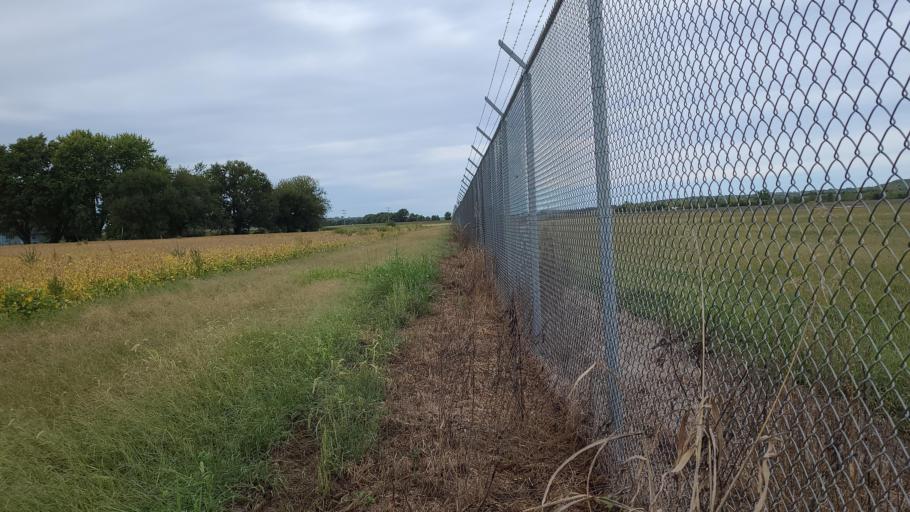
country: US
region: Kansas
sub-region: Douglas County
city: Lawrence
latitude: 39.0182
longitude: -95.2221
